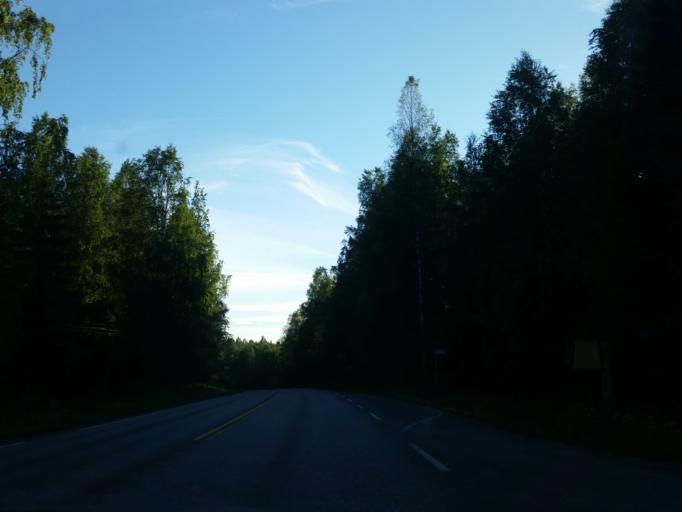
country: FI
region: Northern Savo
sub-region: Kuopio
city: Kuopio
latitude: 62.8475
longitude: 27.3889
